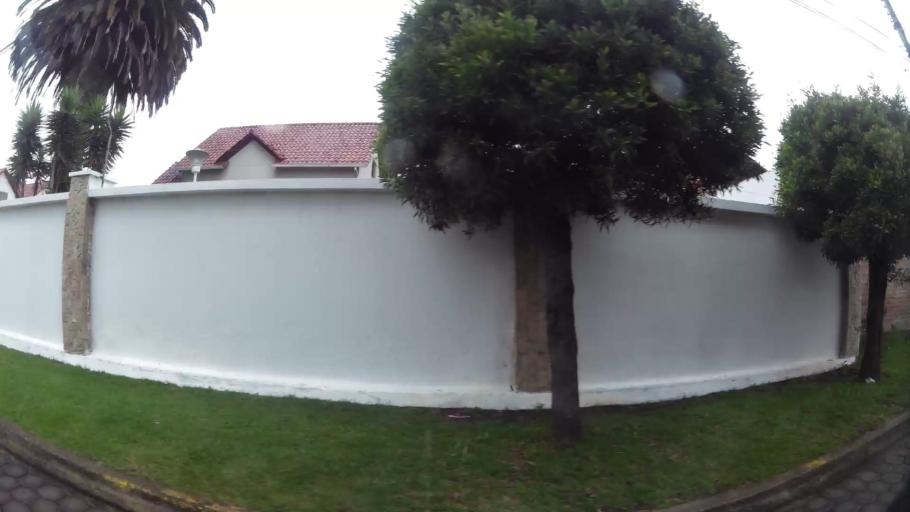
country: EC
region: Pichincha
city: Sangolqui
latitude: -0.2786
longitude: -78.4653
